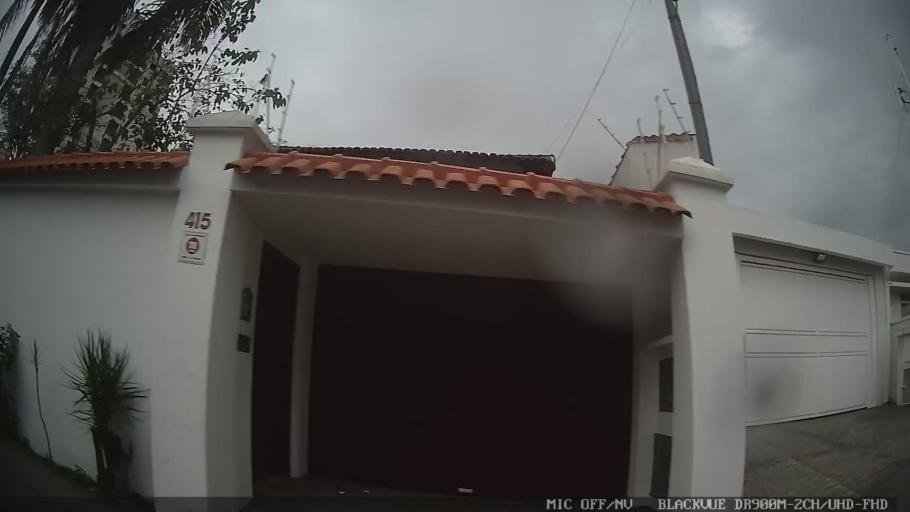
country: BR
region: Sao Paulo
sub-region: Mogi das Cruzes
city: Mogi das Cruzes
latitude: -23.5217
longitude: -46.1767
